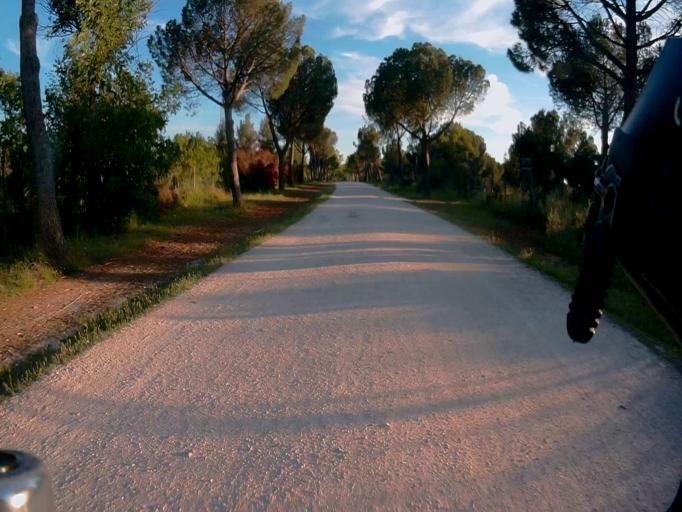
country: ES
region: Madrid
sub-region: Provincia de Madrid
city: Leganes
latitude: 40.3267
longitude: -3.7960
